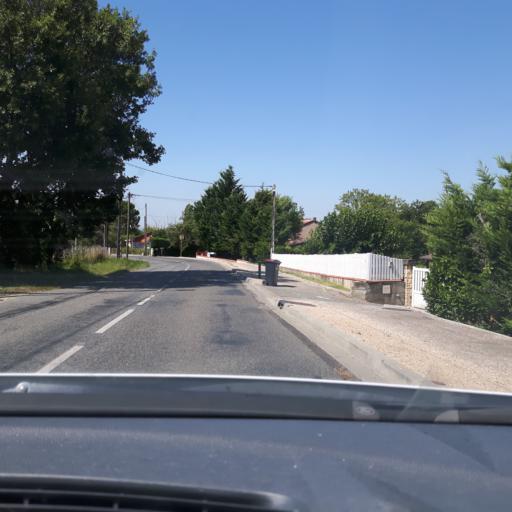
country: FR
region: Midi-Pyrenees
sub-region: Departement de la Haute-Garonne
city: Bouloc
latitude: 43.7775
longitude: 1.3959
